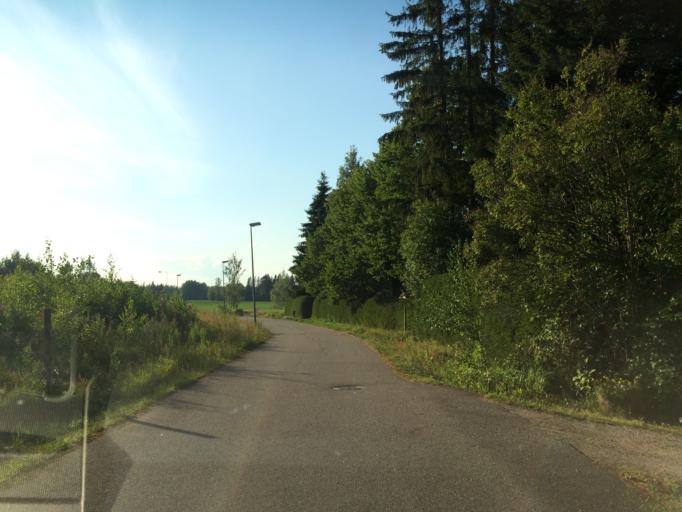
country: FI
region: Haeme
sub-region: Haemeenlinna
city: Parola
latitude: 61.0456
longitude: 24.3795
